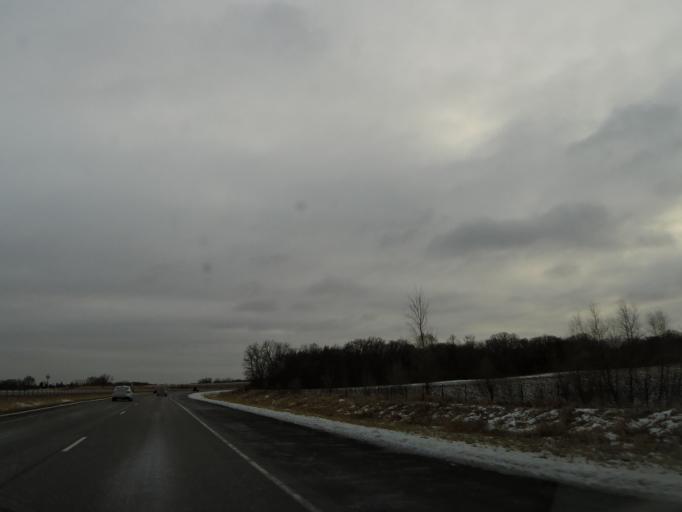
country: US
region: Minnesota
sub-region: Carver County
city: Carver
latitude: 44.7857
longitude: -93.6321
